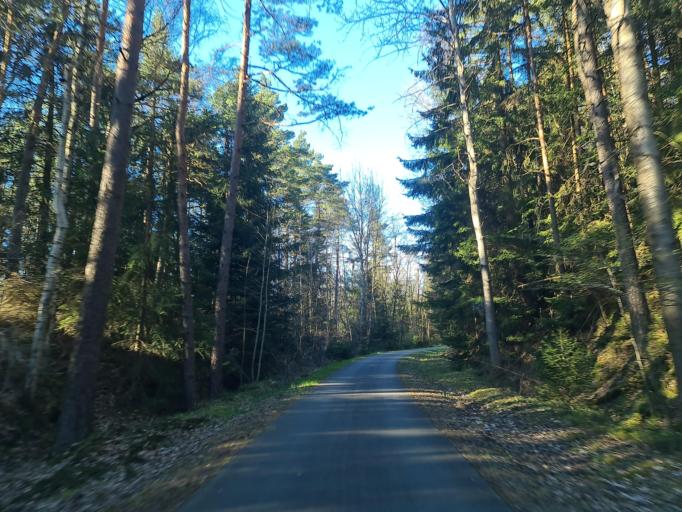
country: DE
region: Saxony
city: Neustadt Vogtland
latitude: 50.4743
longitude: 12.3108
